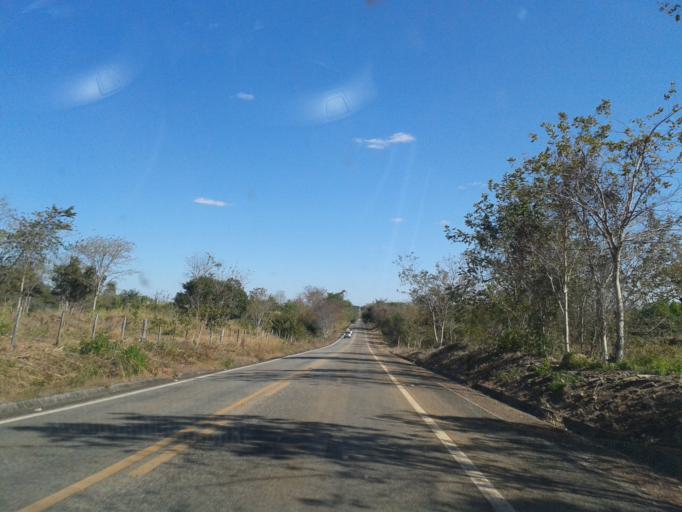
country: BR
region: Goias
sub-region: Mozarlandia
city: Mozarlandia
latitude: -14.5656
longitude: -50.4989
